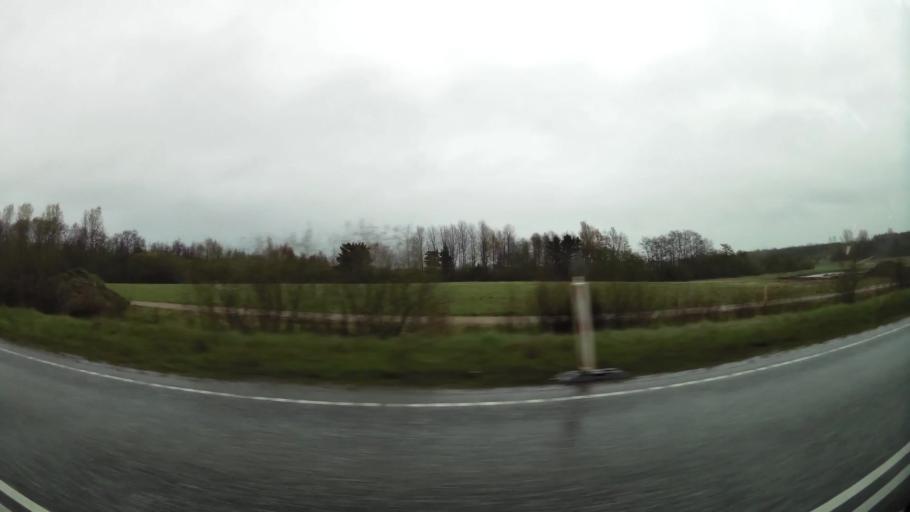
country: DK
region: Central Jutland
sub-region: Herning Kommune
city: Avlum
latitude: 56.2169
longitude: 8.8548
